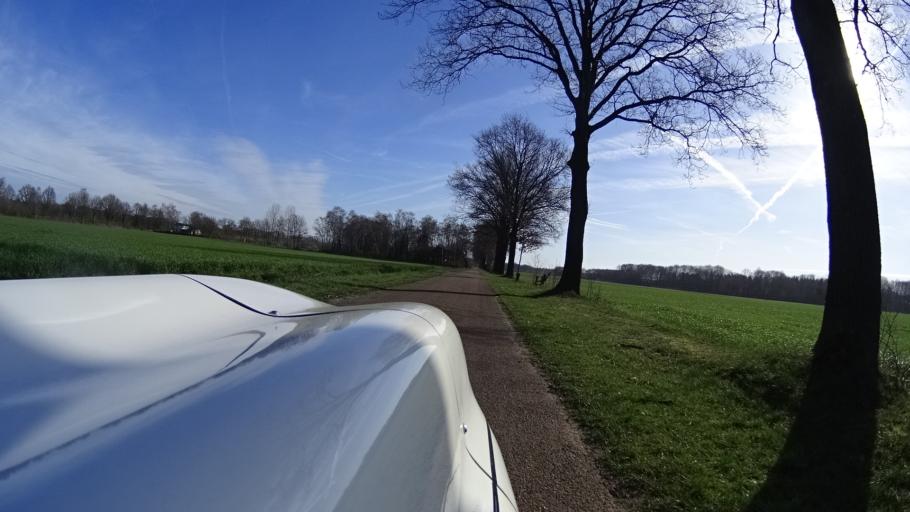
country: NL
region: North Brabant
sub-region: Gemeente Uden
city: Odiliapeel
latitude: 51.6647
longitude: 5.6883
